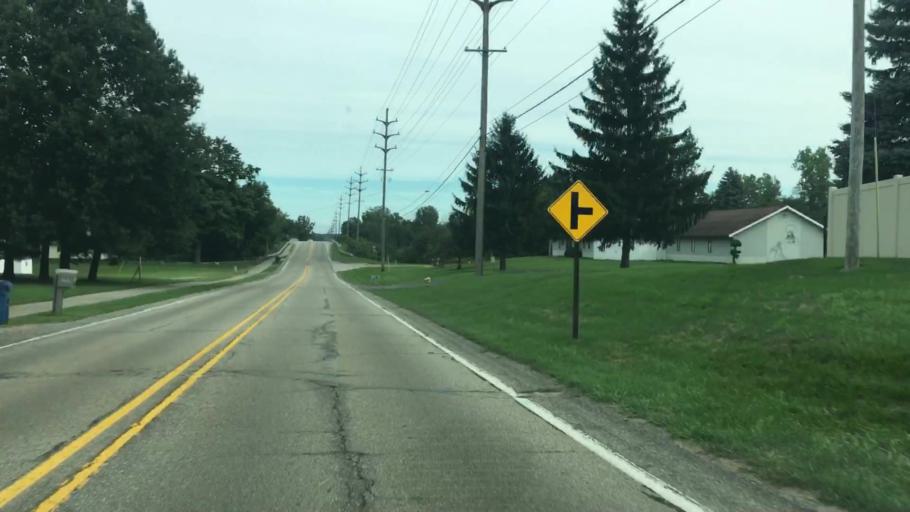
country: US
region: Michigan
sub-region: Ottawa County
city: Jenison
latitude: 42.8744
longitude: -85.7823
